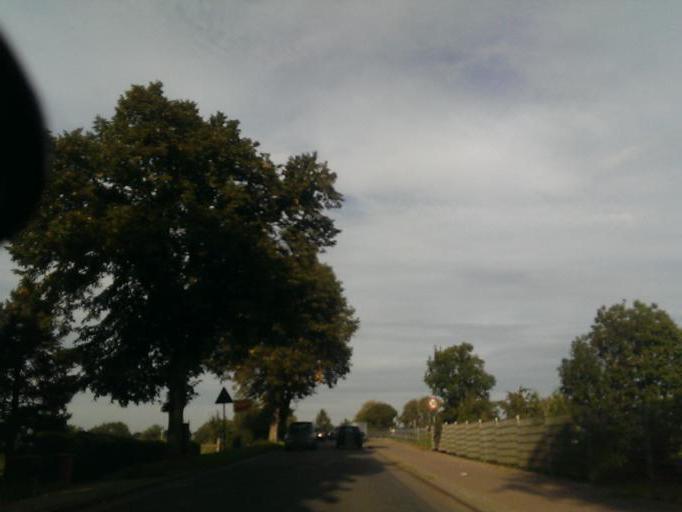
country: DE
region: Lower Saxony
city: Neustadt am Rubenberge
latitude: 52.4620
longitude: 9.4754
